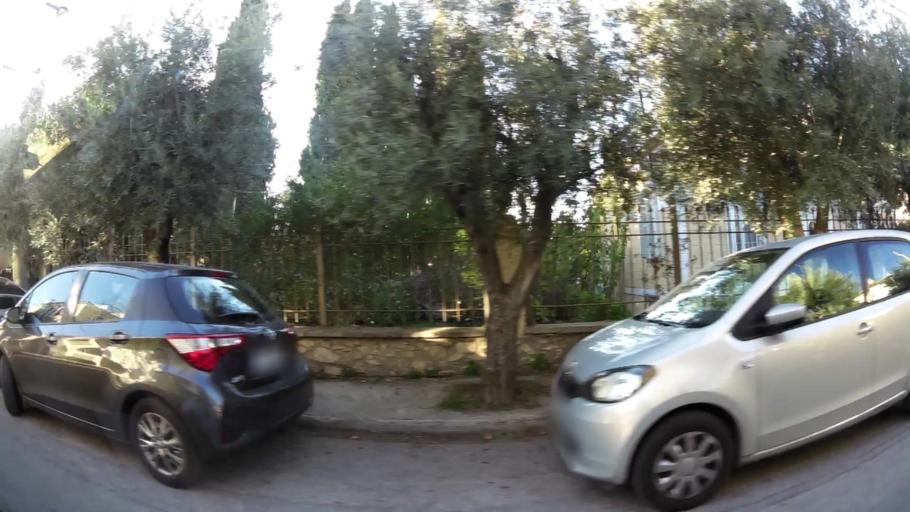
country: GR
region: Attica
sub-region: Nomarchia Athinas
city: Kifisia
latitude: 38.0773
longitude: 23.8042
